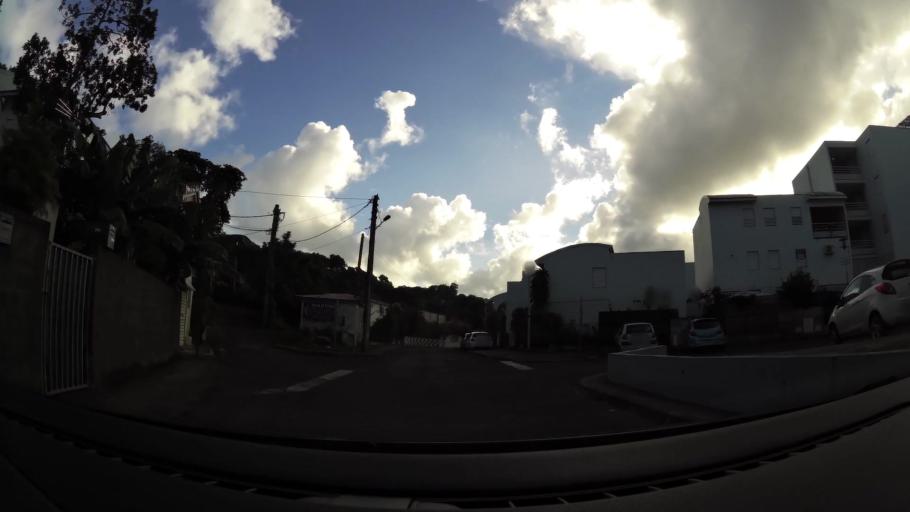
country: GP
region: Guadeloupe
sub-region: Guadeloupe
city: Pointe-a-Pitre
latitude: 16.2428
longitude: -61.5297
